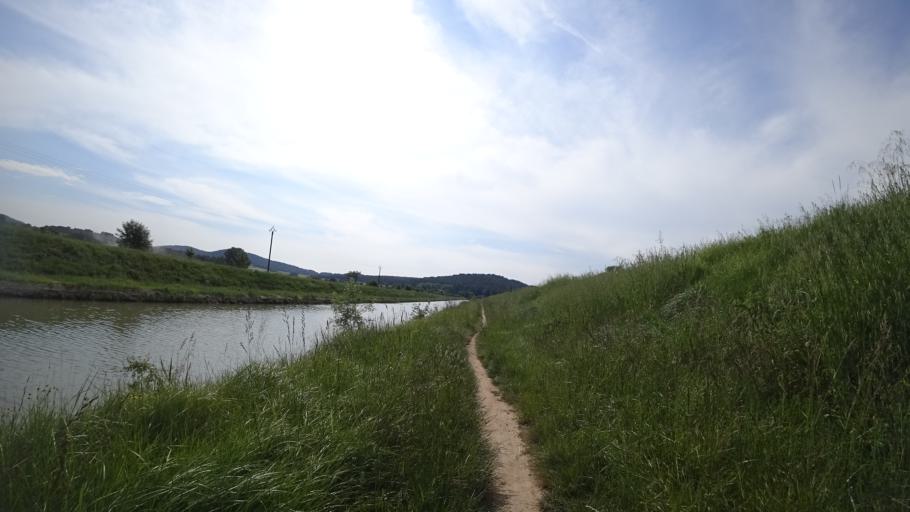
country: FR
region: Languedoc-Roussillon
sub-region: Departement de l'Herault
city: Olonzac
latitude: 43.2656
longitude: 2.7422
